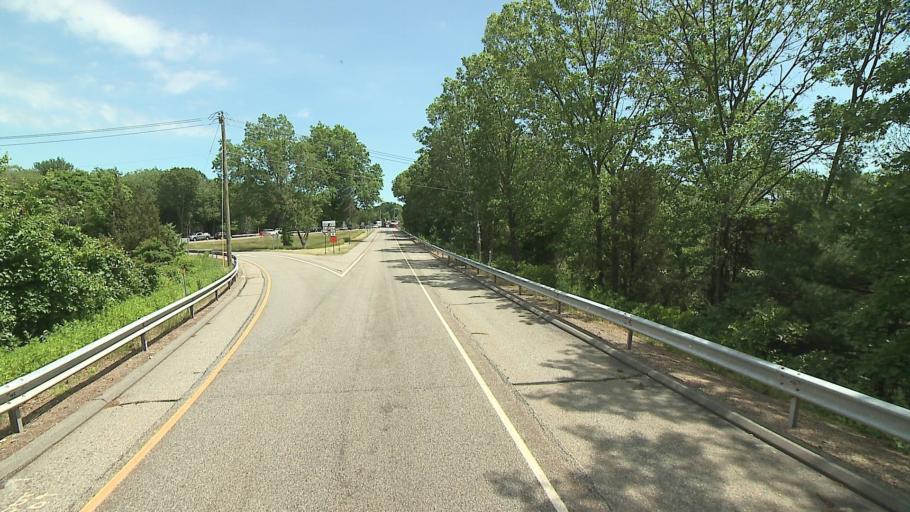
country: US
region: Connecticut
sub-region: Middlesex County
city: Old Saybrook
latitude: 41.3041
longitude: -72.3803
